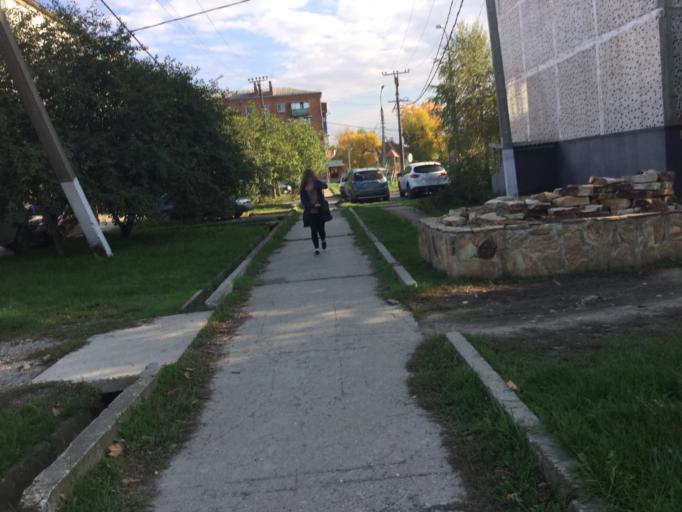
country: RU
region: Krasnodarskiy
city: Slavyansk-na-Kubani
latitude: 45.2558
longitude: 38.1131
